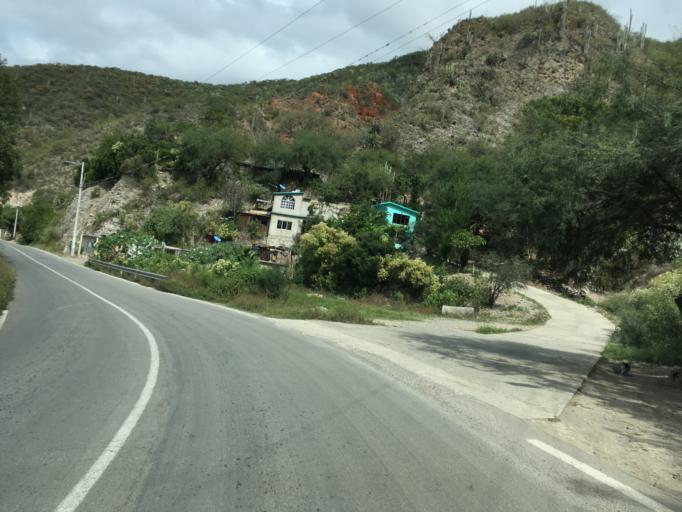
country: MX
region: Hidalgo
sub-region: San Agustin Metzquititlan
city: Mezquititlan
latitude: 20.5311
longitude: -98.7178
